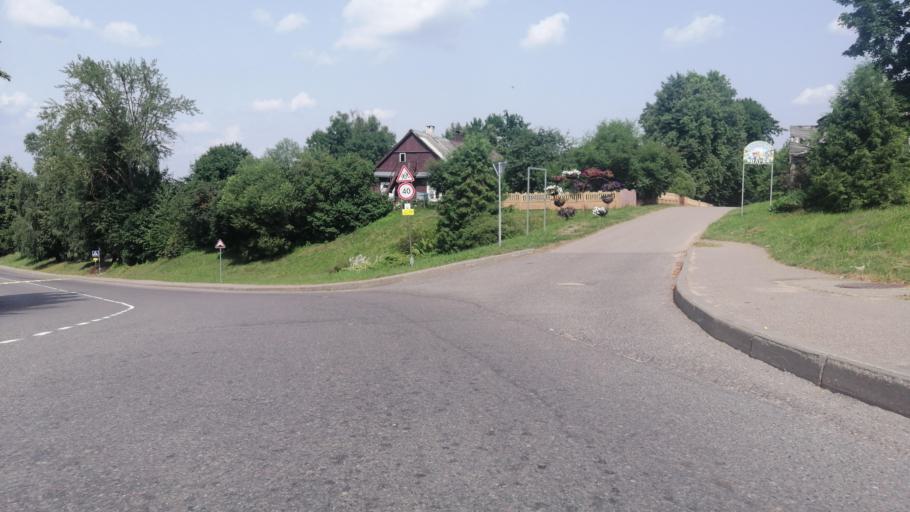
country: BY
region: Grodnenskaya
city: Navahrudak
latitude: 53.6023
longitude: 25.8241
